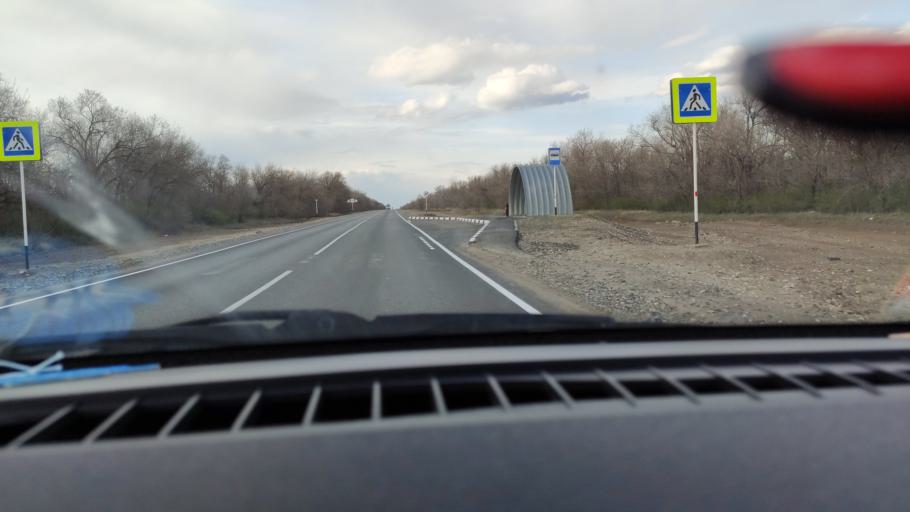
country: RU
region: Saratov
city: Krasnoarmeysk
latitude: 51.1265
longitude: 45.9580
